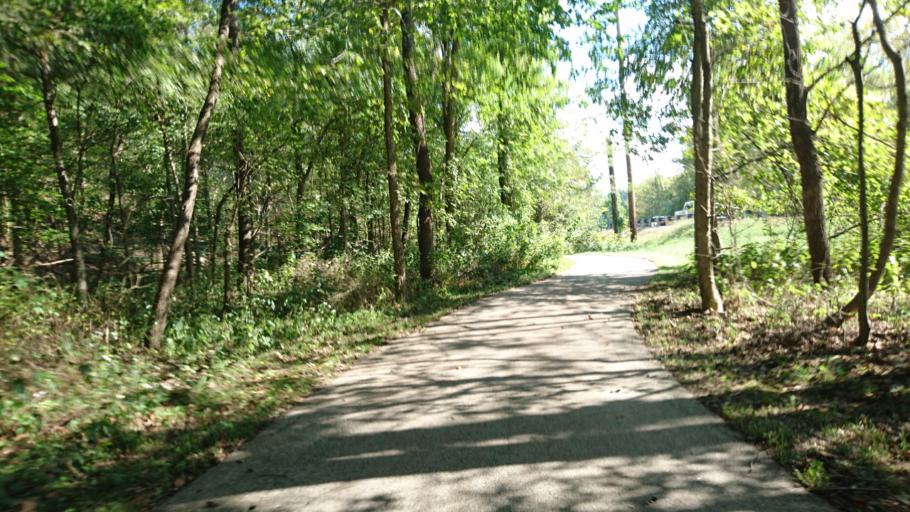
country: US
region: Missouri
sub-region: Saint Louis County
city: Wildwood
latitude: 38.5560
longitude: -90.6422
